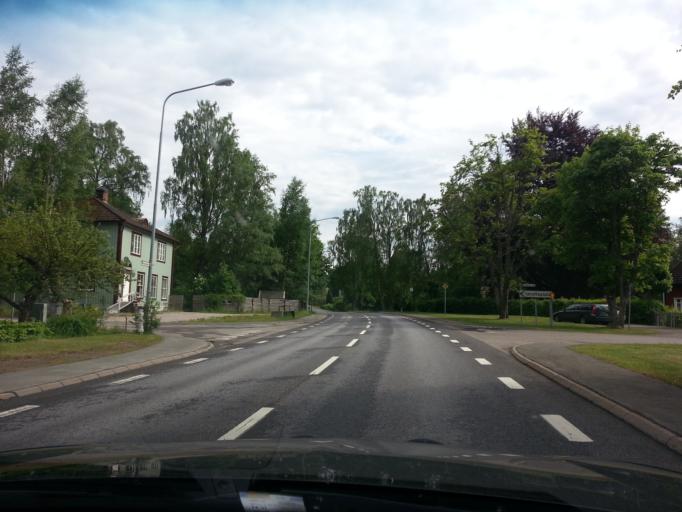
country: SE
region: Joenkoeping
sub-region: Vetlanda Kommun
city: Vetlanda
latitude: 57.3112
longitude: 15.1216
